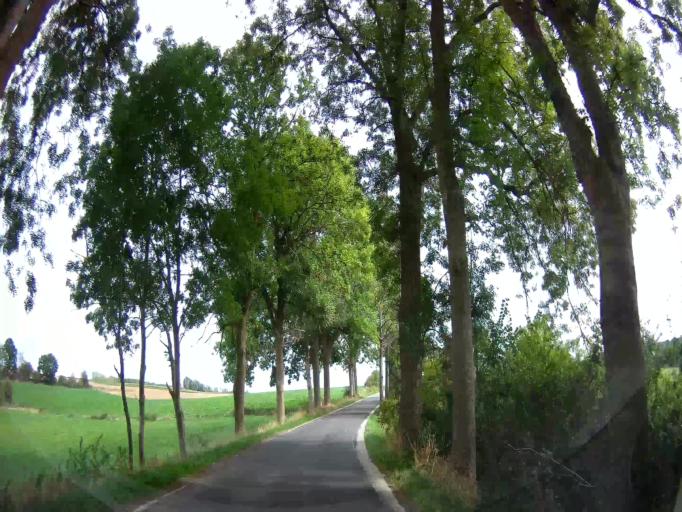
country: BE
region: Wallonia
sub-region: Province de Namur
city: Ohey
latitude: 50.4143
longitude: 5.1797
